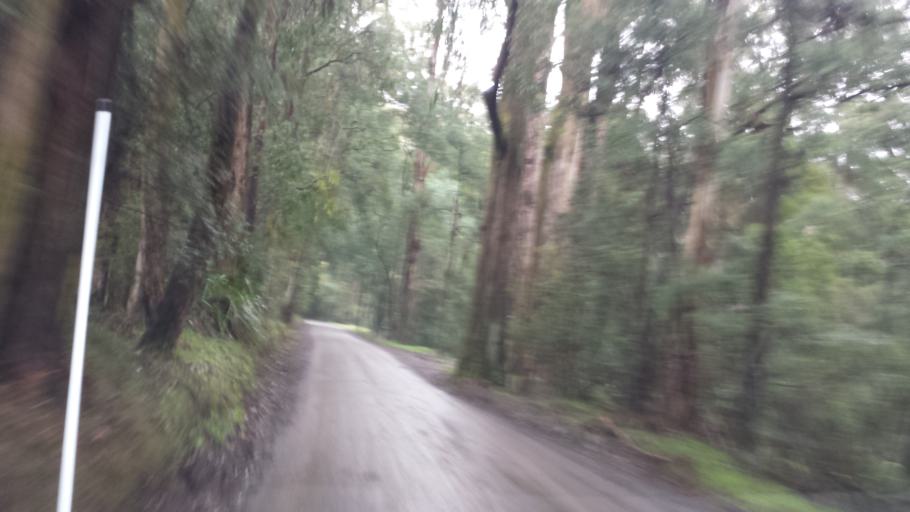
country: AU
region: Victoria
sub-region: Yarra Ranges
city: Monbulk
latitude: -37.8991
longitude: 145.4188
